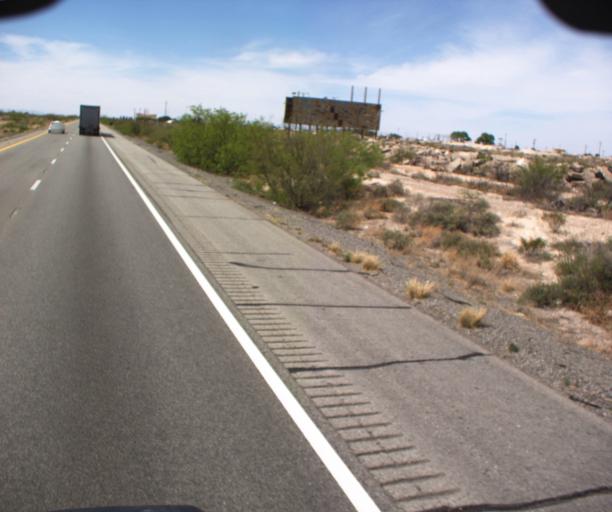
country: US
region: New Mexico
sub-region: Hidalgo County
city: Lordsburg
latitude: 32.2606
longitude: -109.2154
